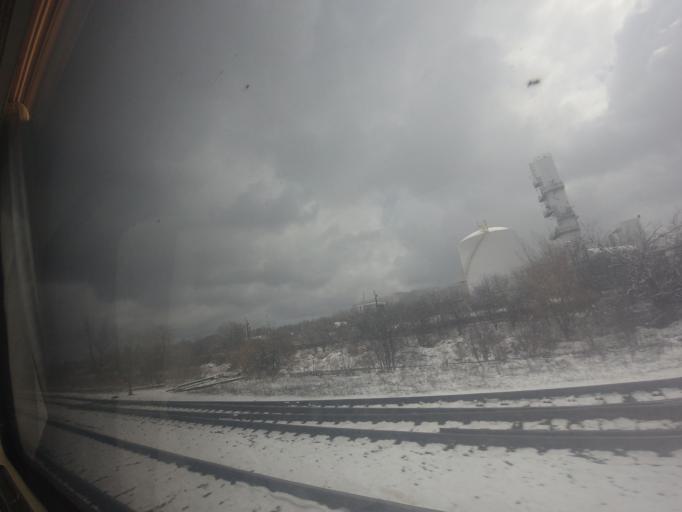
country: CA
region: Ontario
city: Scarborough
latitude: 43.7333
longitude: -79.2420
